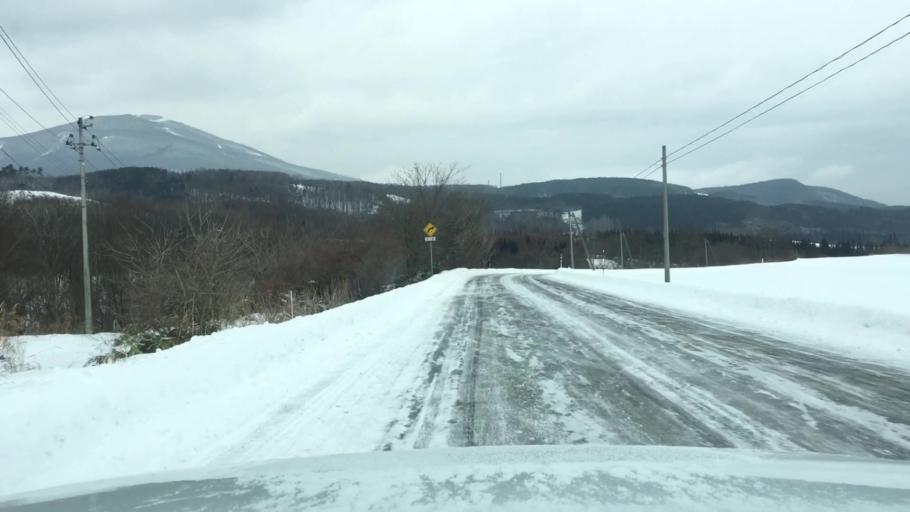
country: JP
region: Iwate
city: Shizukuishi
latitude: 39.9338
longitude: 141.0018
